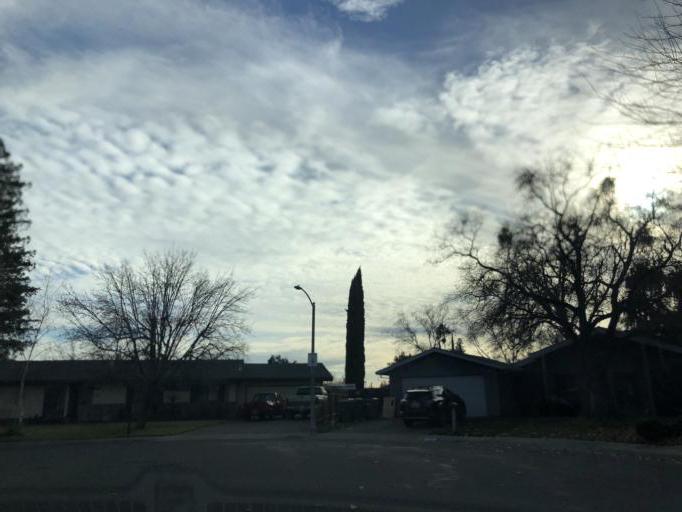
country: US
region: California
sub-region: Yolo County
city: Woodland
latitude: 38.6707
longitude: -121.7581
